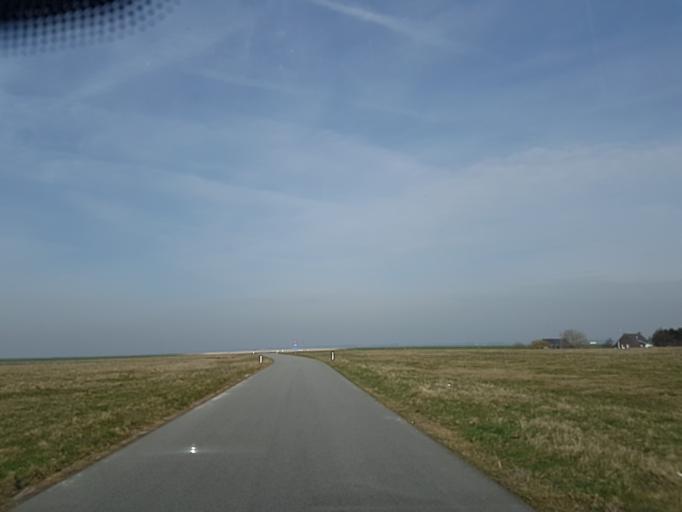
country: NL
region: Zeeland
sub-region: Gemeente Reimerswaal
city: Yerseke
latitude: 51.3961
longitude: 4.0156
